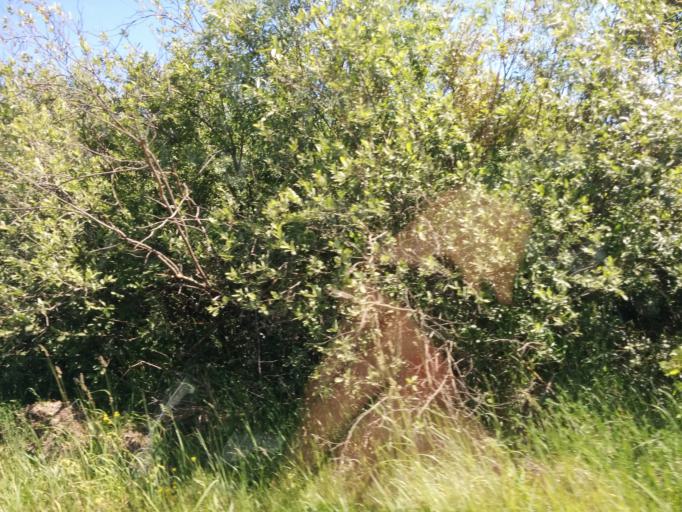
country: RU
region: Tambov
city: Morshansk
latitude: 53.6142
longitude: 41.8413
